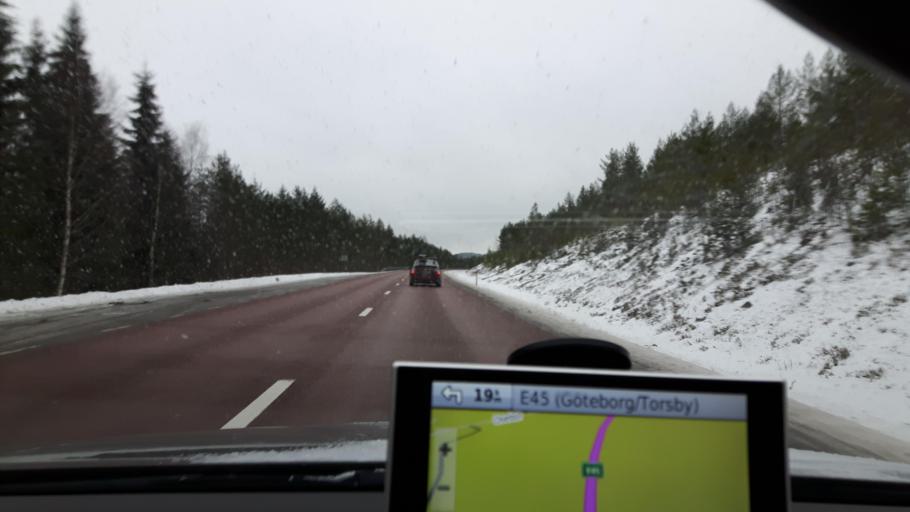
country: SE
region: Vaermland
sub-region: Hagfors Kommun
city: Ekshaerad
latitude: 60.3997
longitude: 13.2619
